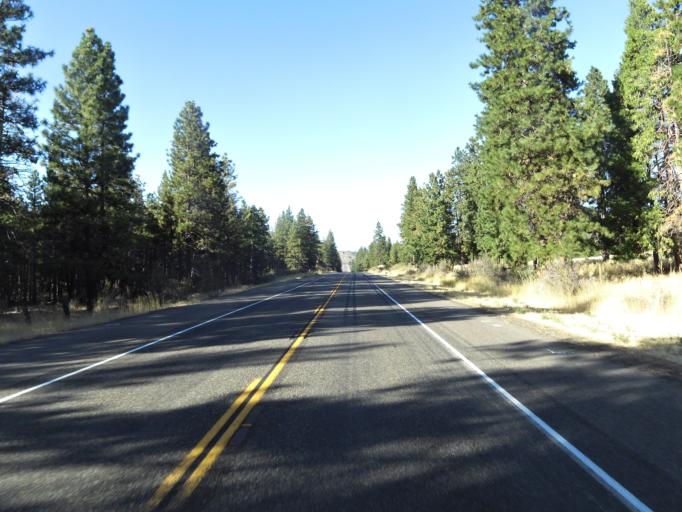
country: US
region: California
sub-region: Siskiyou County
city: Weed
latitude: 41.4599
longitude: -122.3565
